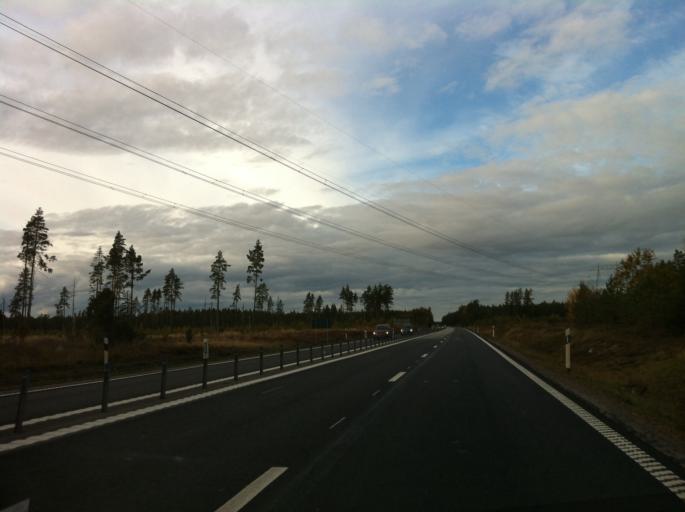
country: SE
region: OErebro
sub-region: Askersunds Kommun
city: Asbro
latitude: 58.9878
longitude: 15.0400
